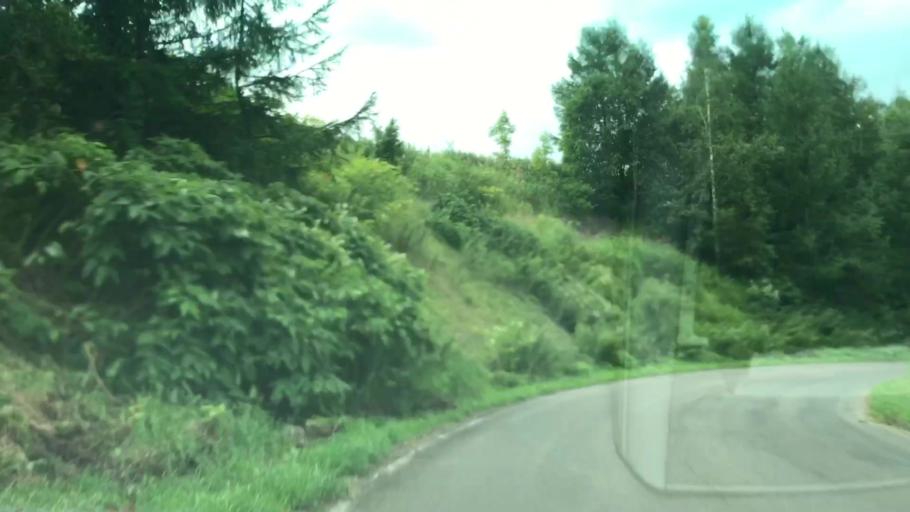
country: JP
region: Hokkaido
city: Yoichi
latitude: 43.1727
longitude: 140.8379
